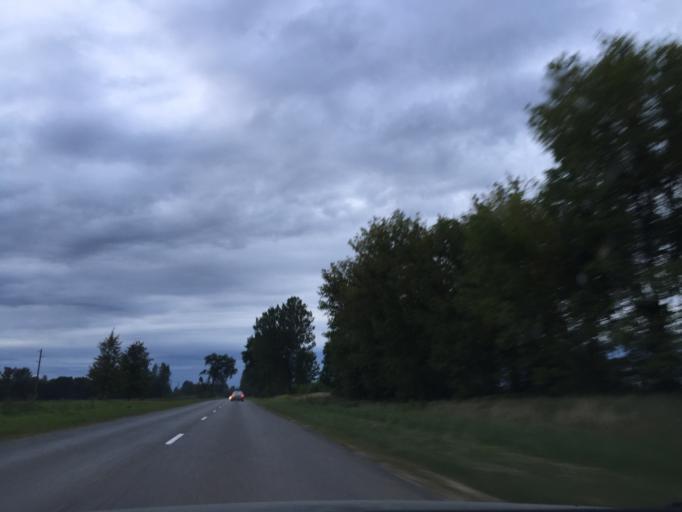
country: LV
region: Vecumnieki
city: Vecumnieki
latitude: 56.5482
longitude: 24.5442
